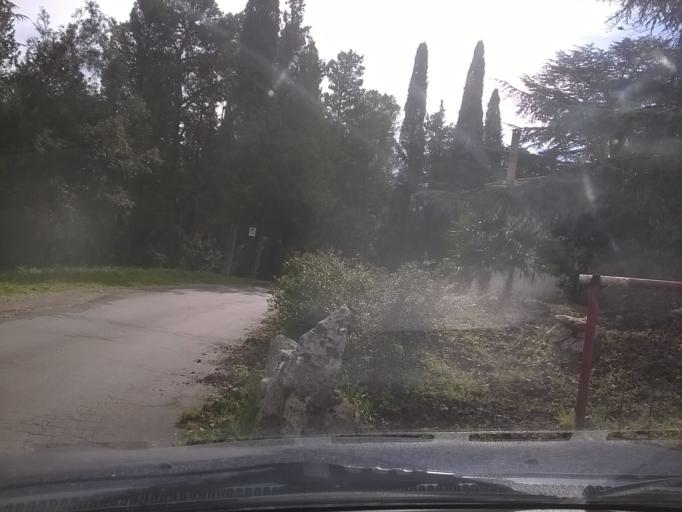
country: IT
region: Apulia
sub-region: Provincia di Bari
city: Cassano delle Murge
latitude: 40.8948
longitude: 16.7006
